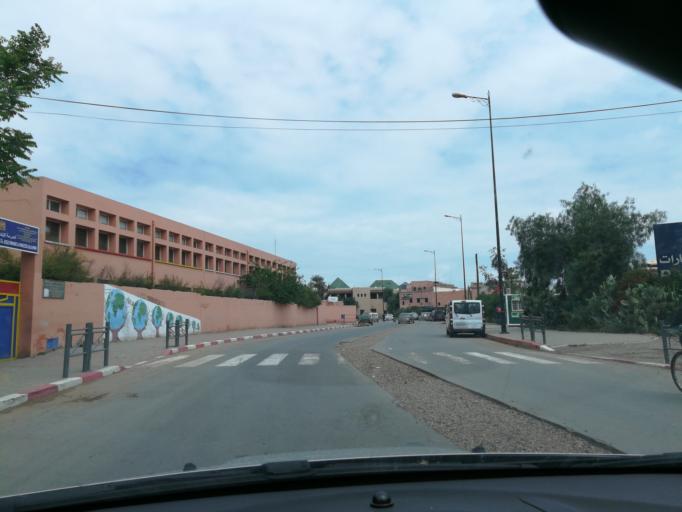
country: MA
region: Marrakech-Tensift-Al Haouz
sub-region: Marrakech
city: Marrakesh
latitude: 31.6305
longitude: -7.9981
